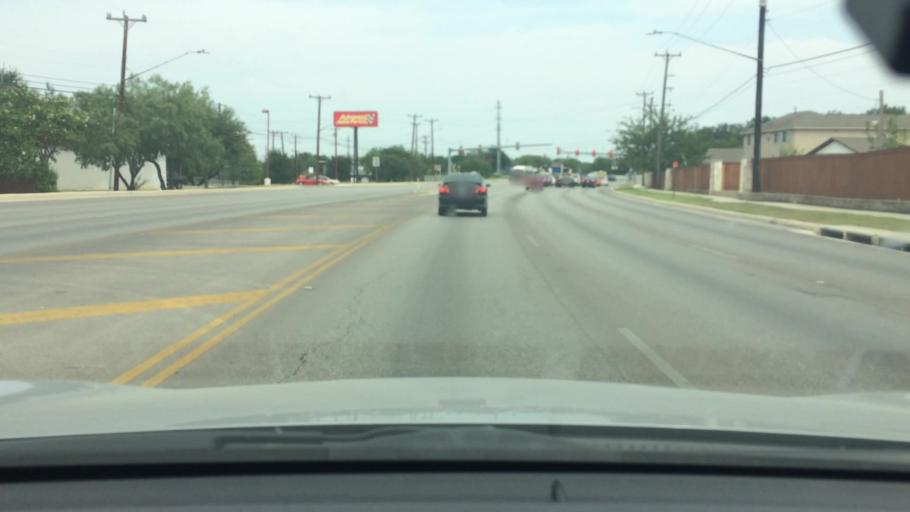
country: US
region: Texas
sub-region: Bexar County
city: Leon Valley
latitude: 29.4752
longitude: -98.6564
